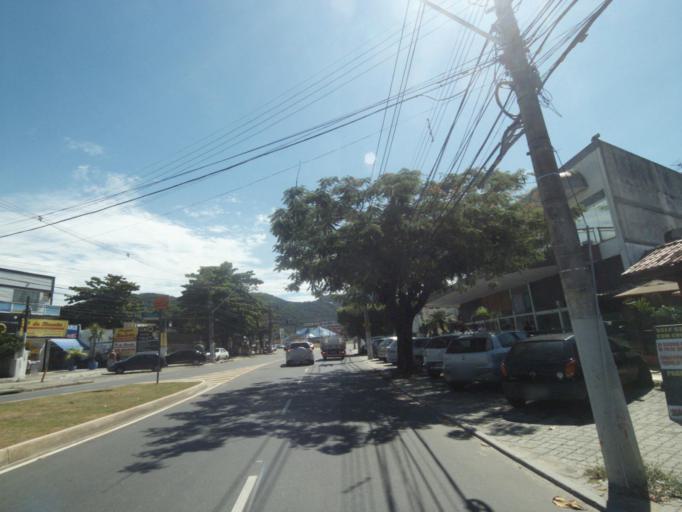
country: BR
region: Rio de Janeiro
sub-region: Niteroi
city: Niteroi
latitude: -22.9433
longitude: -43.0577
